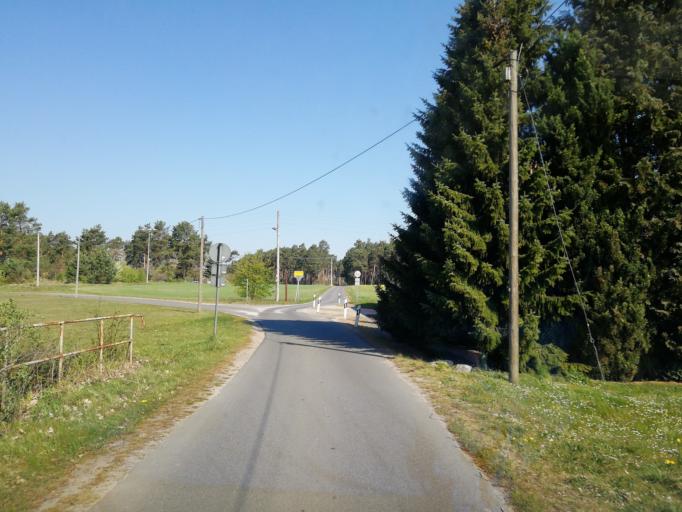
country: DE
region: Brandenburg
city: Sallgast
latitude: 51.6490
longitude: 13.8578
